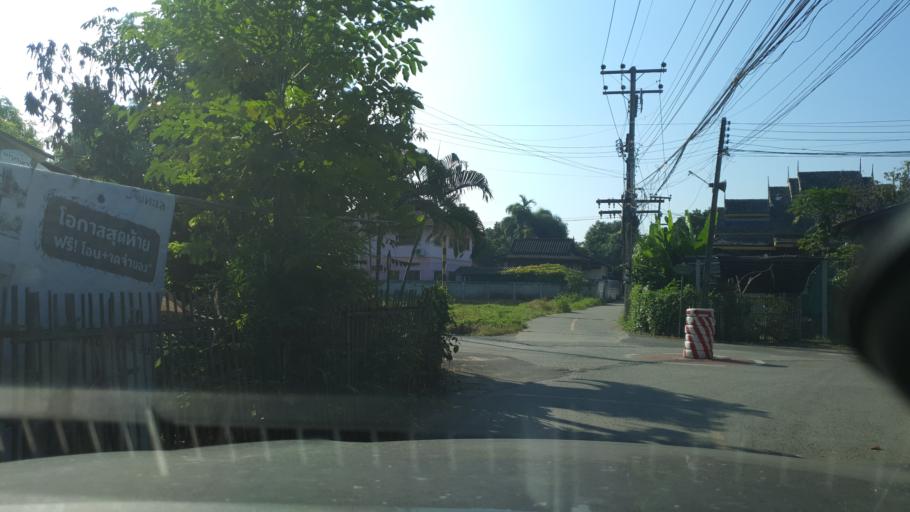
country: TH
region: Chiang Mai
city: San Kamphaeng
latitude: 18.7512
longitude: 99.1452
